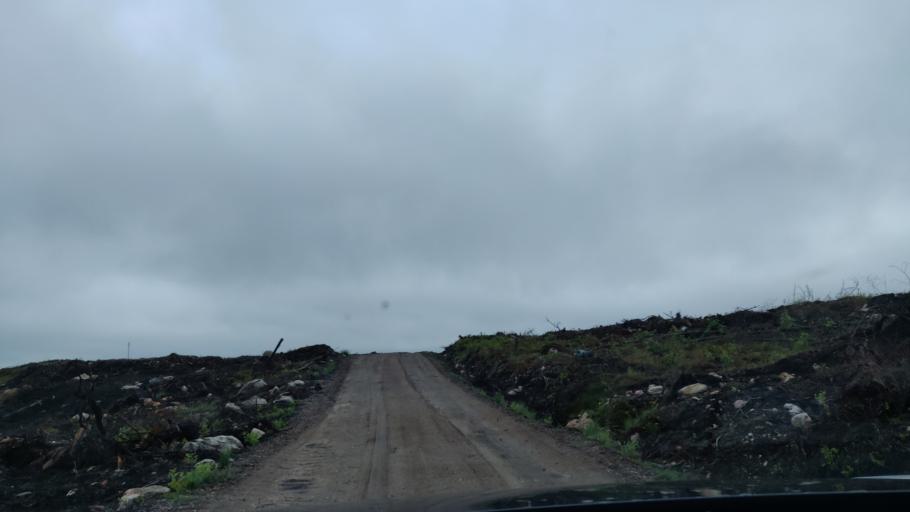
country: SE
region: Dalarna
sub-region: Avesta Kommun
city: Horndal
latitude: 60.3164
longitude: 16.3988
